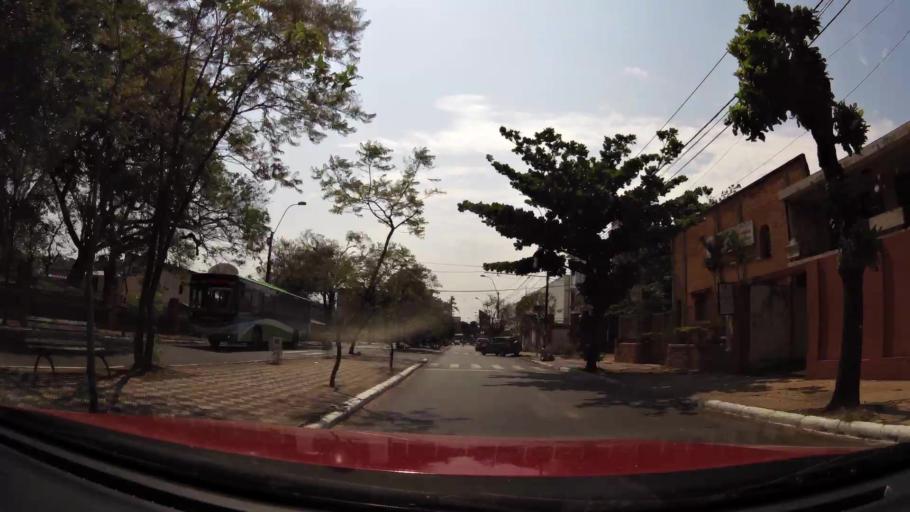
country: PY
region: Asuncion
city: Asuncion
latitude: -25.2882
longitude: -57.6501
